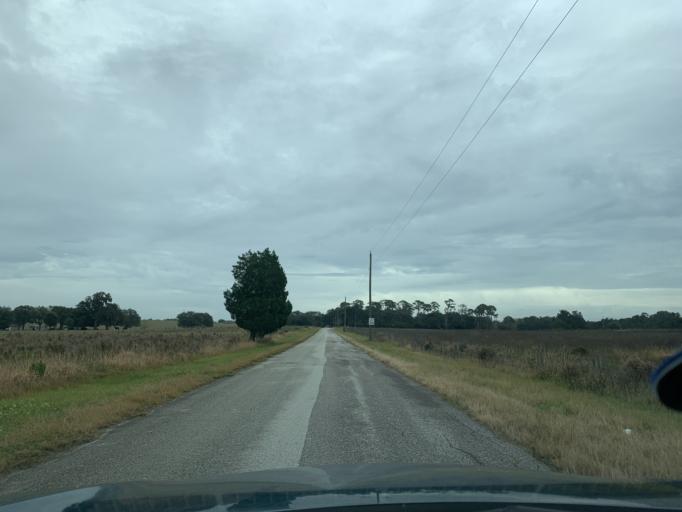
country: US
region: Florida
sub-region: Pasco County
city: San Antonio
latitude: 28.3246
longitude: -82.2739
